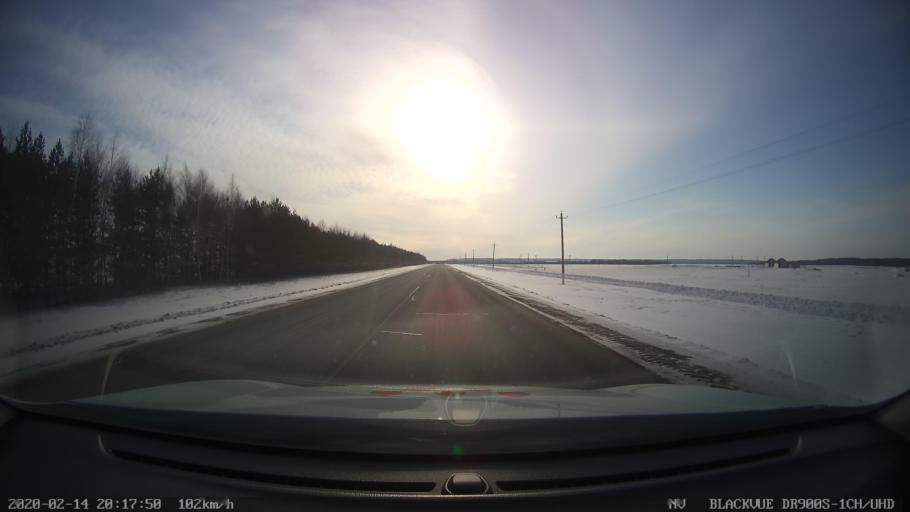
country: RU
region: Tatarstan
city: Verkhniy Uslon
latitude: 55.5950
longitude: 48.8810
